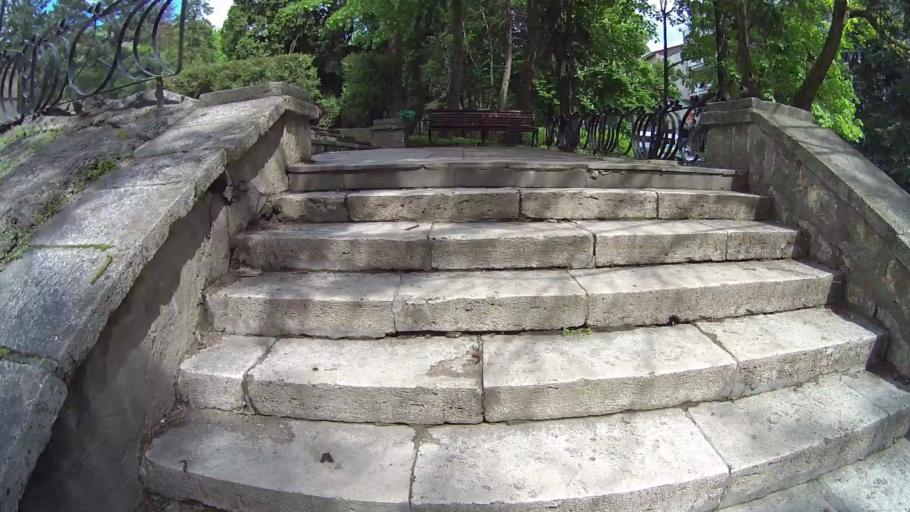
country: RU
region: Stavropol'skiy
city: Pyatigorsk
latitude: 44.0408
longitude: 43.0793
